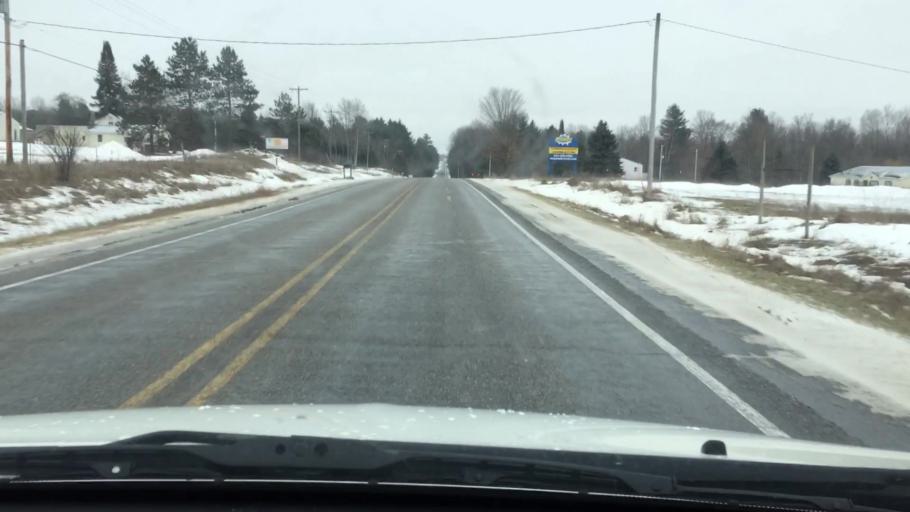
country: US
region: Michigan
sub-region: Wexford County
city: Cadillac
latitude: 44.0618
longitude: -85.4440
